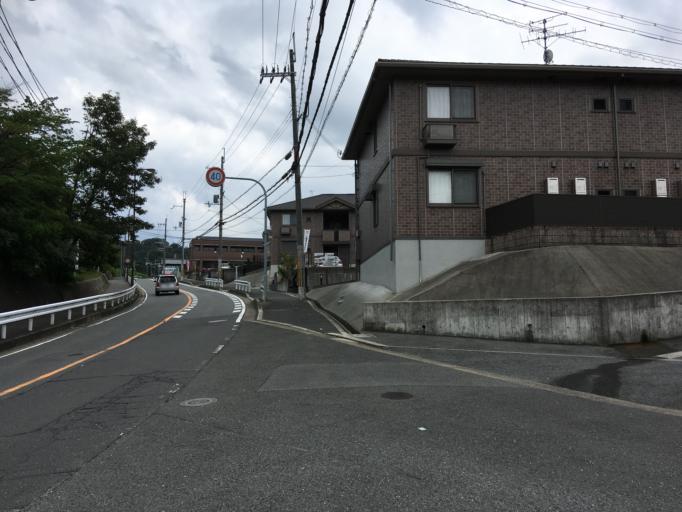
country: JP
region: Nara
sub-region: Ikoma-shi
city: Ikoma
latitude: 34.6662
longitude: 135.7164
